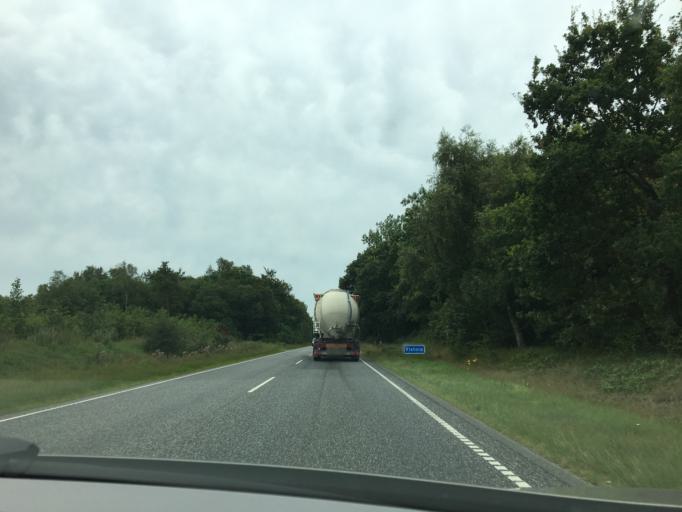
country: DK
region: Central Jutland
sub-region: Herning Kommune
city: Sunds
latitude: 56.3172
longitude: 8.9935
